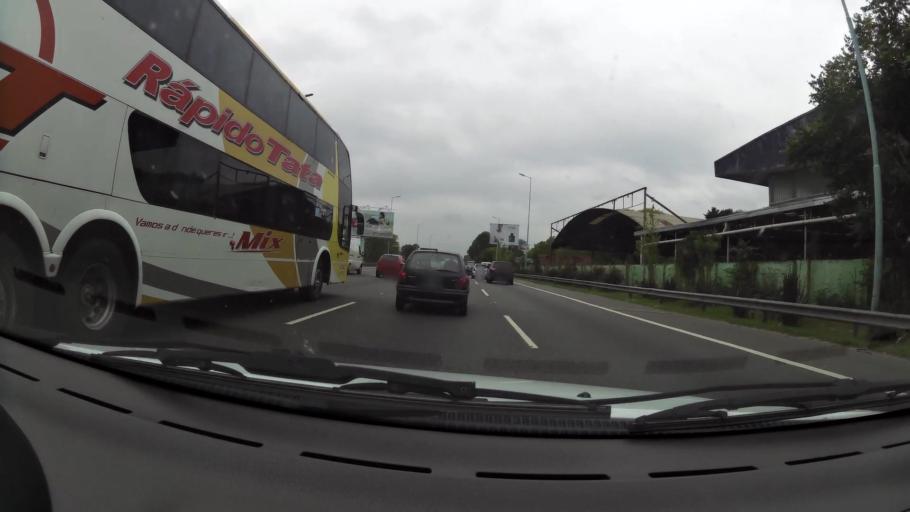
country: AR
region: Buenos Aires F.D.
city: Colegiales
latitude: -34.5451
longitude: -58.4450
